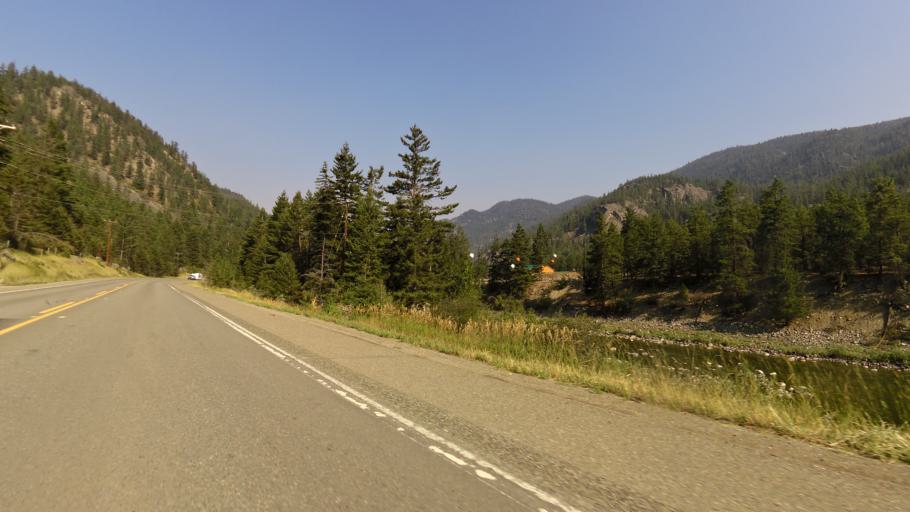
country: CA
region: British Columbia
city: Princeton
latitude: 49.3836
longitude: -120.1957
